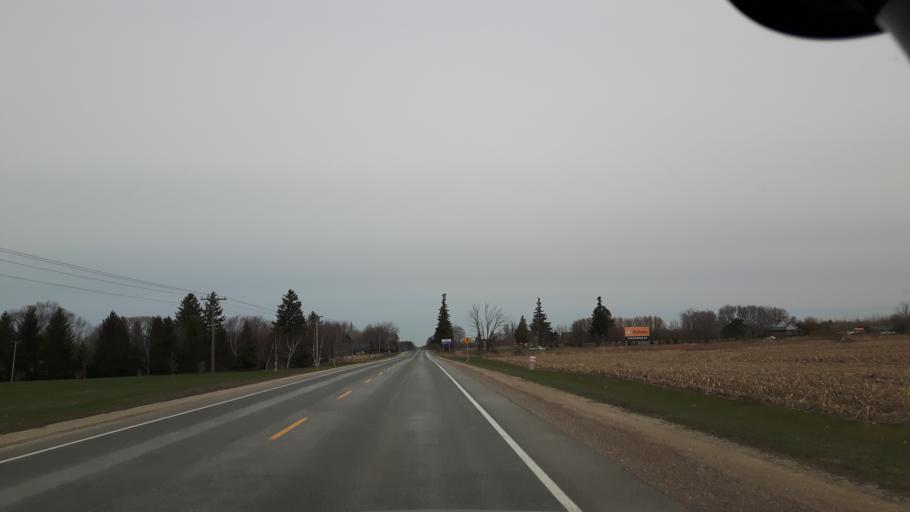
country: CA
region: Ontario
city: Goderich
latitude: 43.6948
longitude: -81.7056
